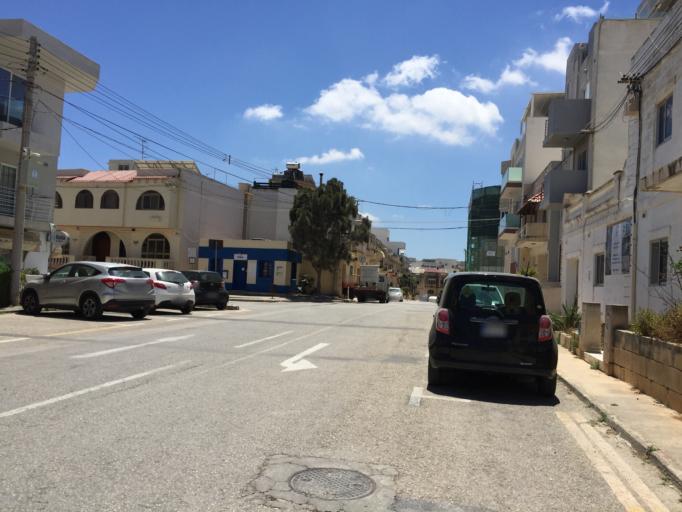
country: MT
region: Is-Swieqi
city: Swieqi
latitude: 35.9219
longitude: 14.4823
